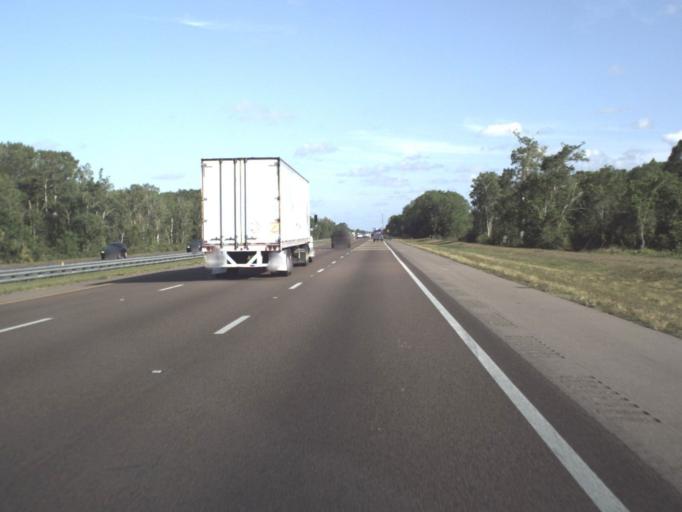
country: US
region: Florida
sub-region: Indian River County
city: Fellsmere
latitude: 27.8513
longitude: -80.5816
